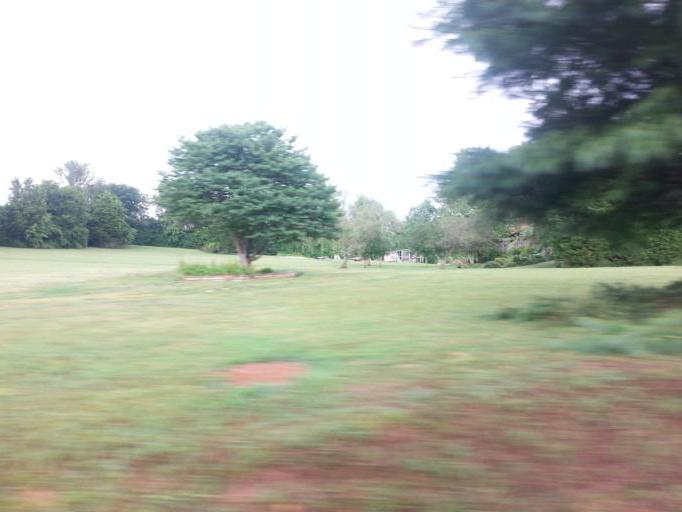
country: US
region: Tennessee
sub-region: Blount County
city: Wildwood
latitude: 35.8320
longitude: -83.8466
